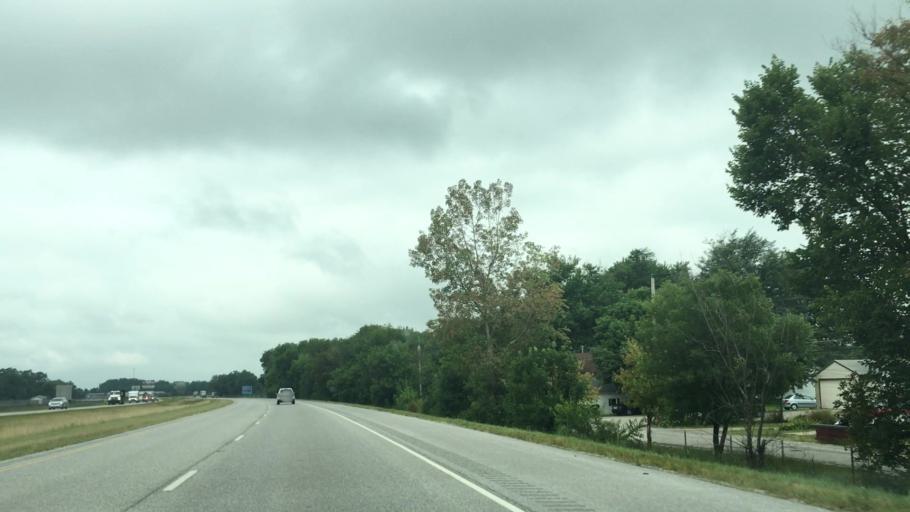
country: US
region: Illinois
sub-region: Rock Island County
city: Moline
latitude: 41.4580
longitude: -90.5128
